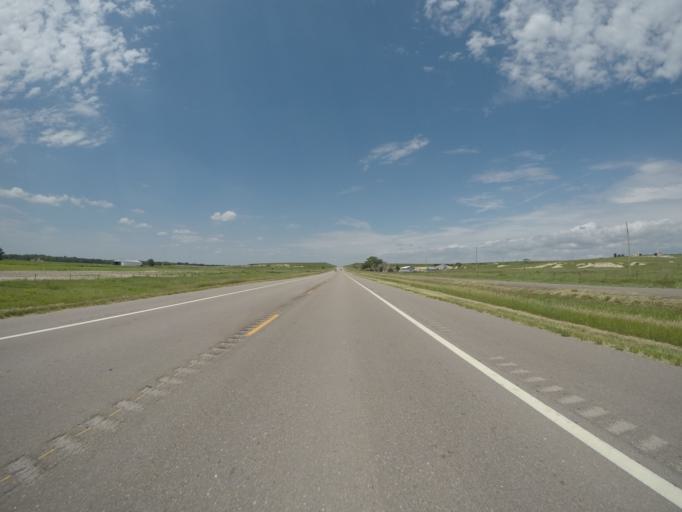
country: US
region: Kansas
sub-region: Graham County
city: Hill City
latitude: 39.3795
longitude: -99.6931
